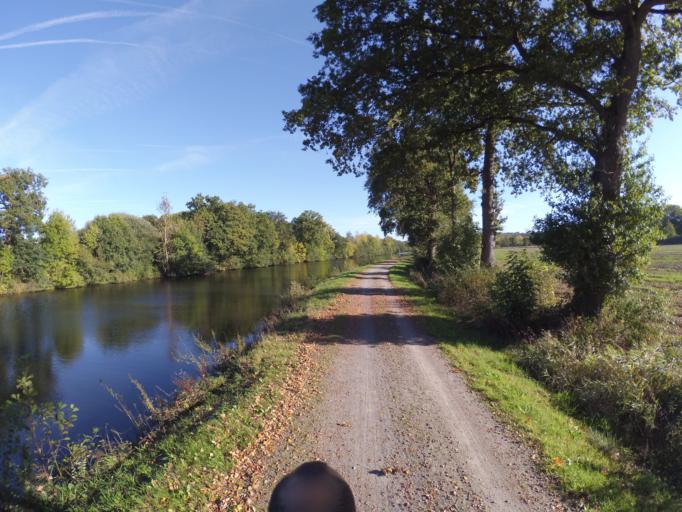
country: FR
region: Brittany
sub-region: Departement du Morbihan
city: Peillac
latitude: 47.7364
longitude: -2.2268
